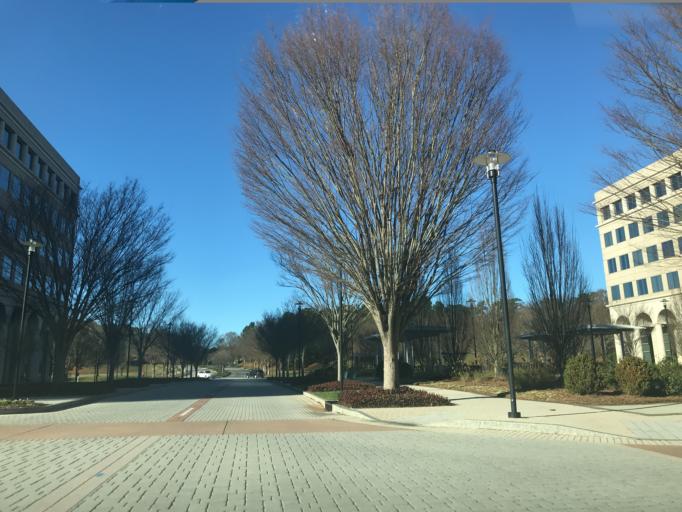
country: US
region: North Carolina
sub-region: Wake County
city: West Raleigh
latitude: 35.8354
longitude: -78.6887
